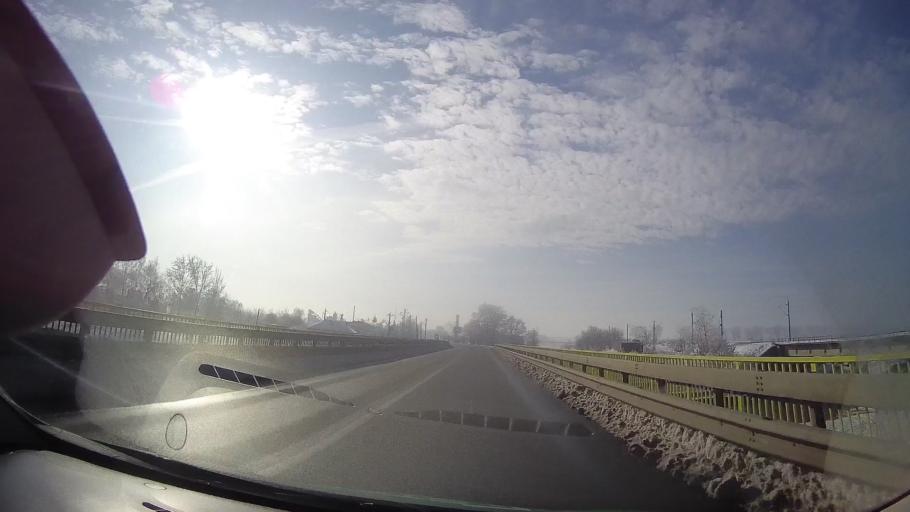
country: RO
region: Neamt
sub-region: Comuna Timisesti
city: Timisesti
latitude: 47.2460
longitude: 26.5440
